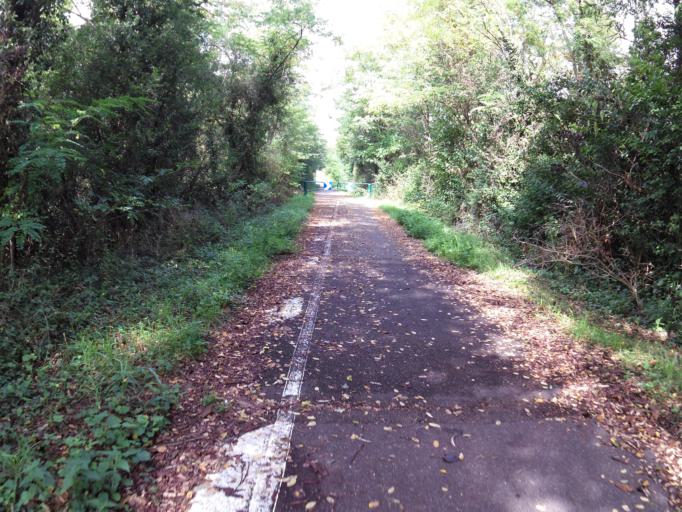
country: FR
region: Alsace
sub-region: Departement du Haut-Rhin
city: Biesheim
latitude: 48.0543
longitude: 7.5497
